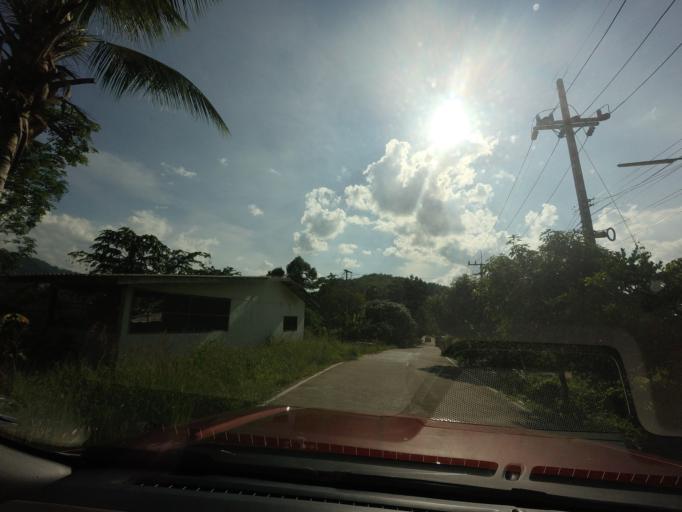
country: TH
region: Yala
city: Than To
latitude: 6.0925
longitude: 101.3169
